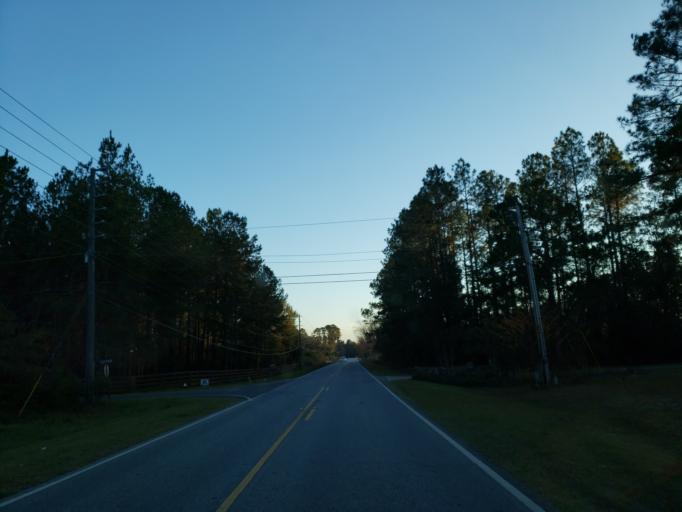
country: US
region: Georgia
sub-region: Crisp County
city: Cordele
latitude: 31.9331
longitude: -83.7662
